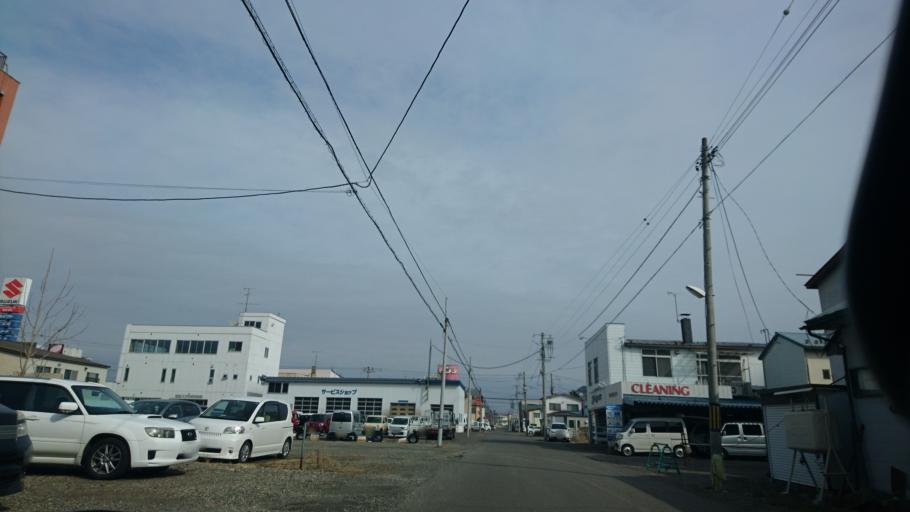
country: JP
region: Hokkaido
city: Obihiro
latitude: 42.9264
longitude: 143.2056
